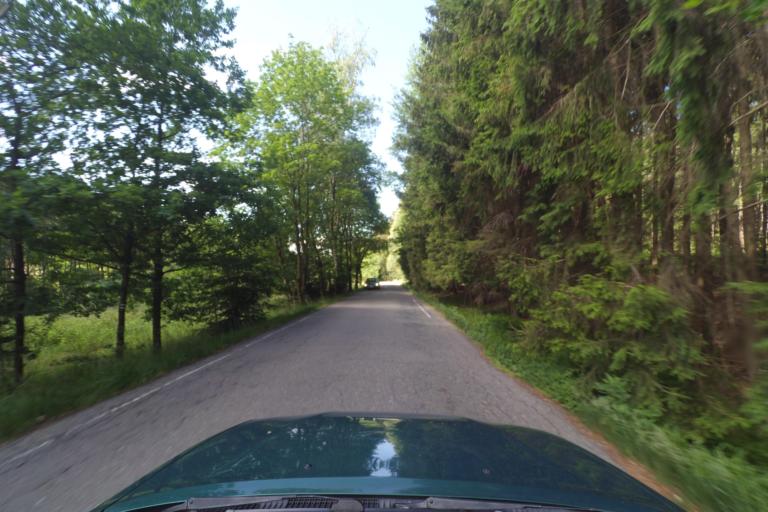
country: CZ
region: Kralovehradecky
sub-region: Okres Nachod
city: Cerveny Kostelec
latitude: 50.4442
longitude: 16.1164
